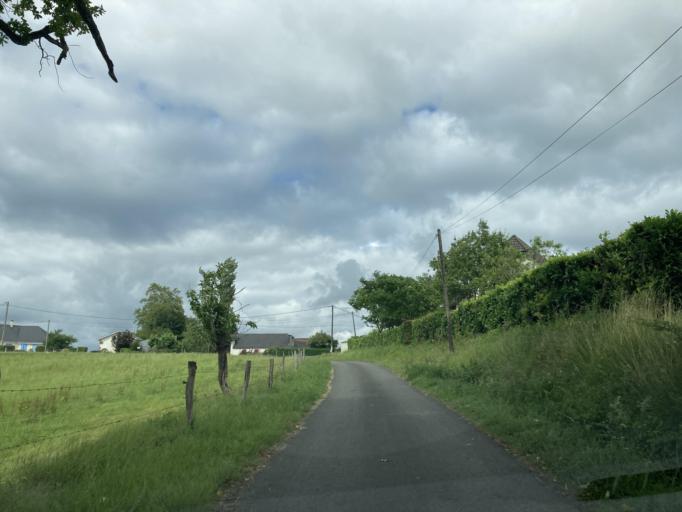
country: FR
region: Aquitaine
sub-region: Departement des Pyrenees-Atlantiques
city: Lucq-de-Bearn
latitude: 43.2651
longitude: -0.6306
